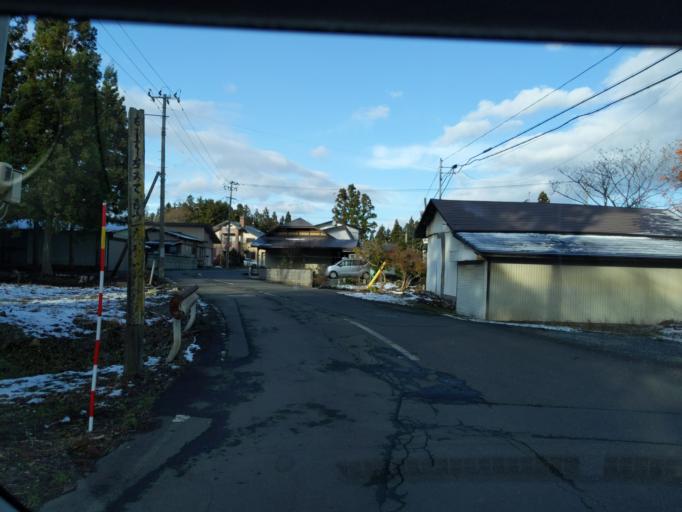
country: JP
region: Iwate
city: Kitakami
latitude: 39.2345
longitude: 141.0510
